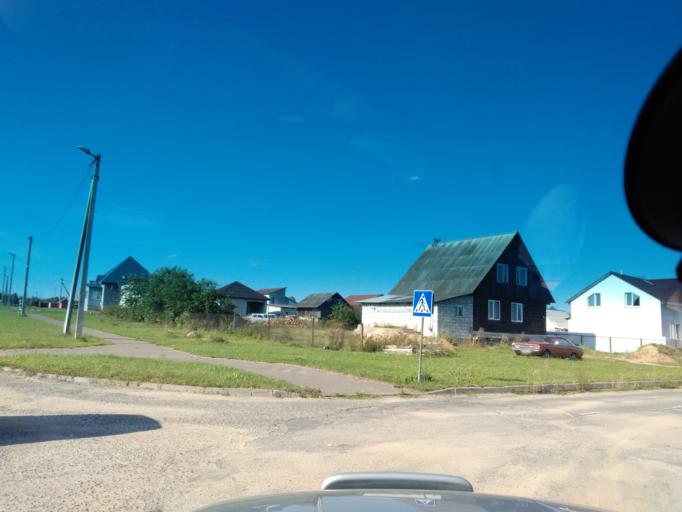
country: BY
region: Minsk
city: Uzda
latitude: 53.4680
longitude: 27.1931
